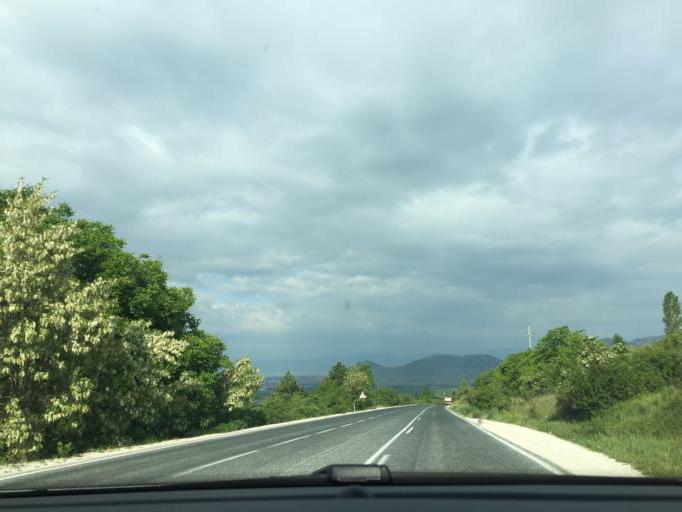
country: MK
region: Prilep
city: Prilep
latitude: 41.3688
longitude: 21.6394
